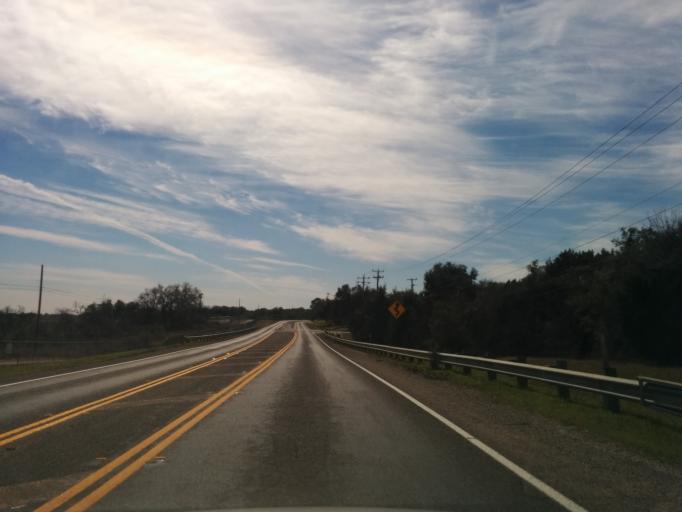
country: US
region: Texas
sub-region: Bexar County
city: Fair Oaks Ranch
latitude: 29.7216
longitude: -98.6237
